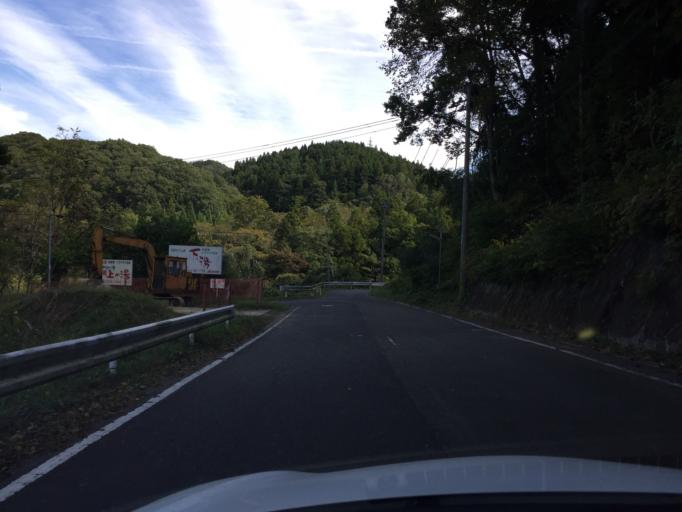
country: JP
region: Fukushima
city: Miharu
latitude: 37.3896
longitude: 140.4537
